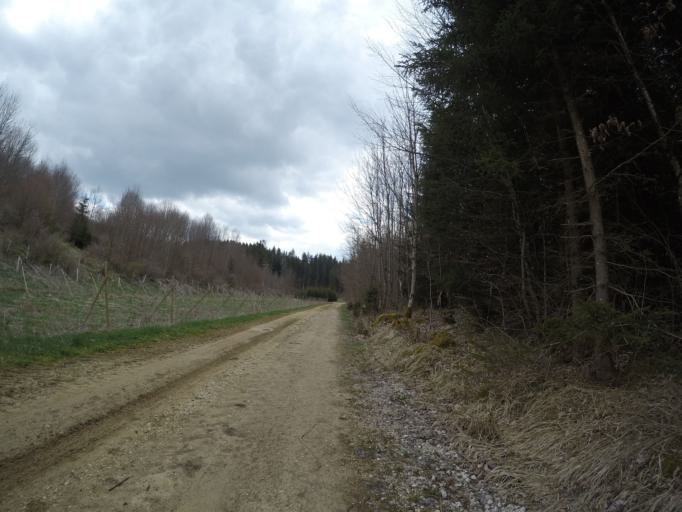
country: DE
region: Baden-Wuerttemberg
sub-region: Tuebingen Region
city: Nellingen
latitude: 48.5002
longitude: 9.7991
